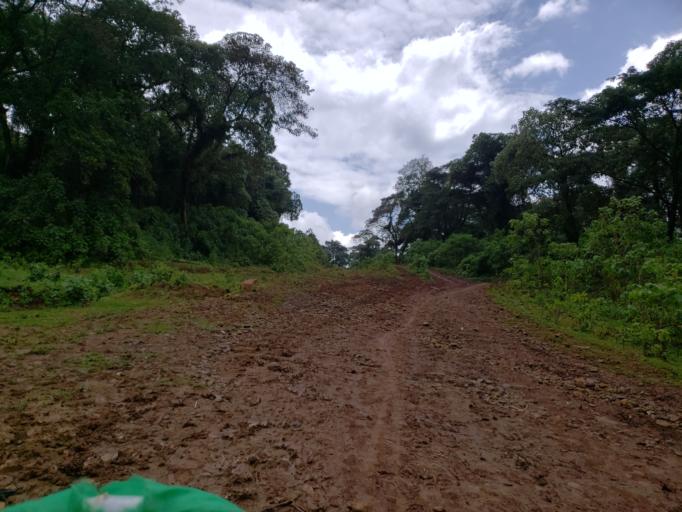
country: ET
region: Oromiya
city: Dodola
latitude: 6.4887
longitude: 39.4979
